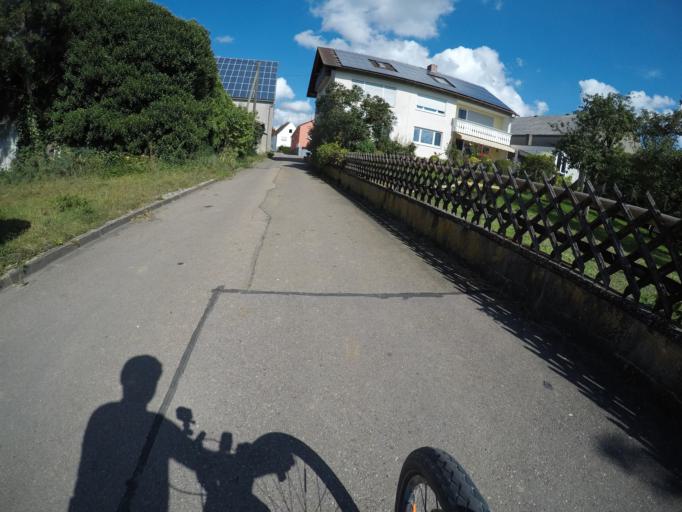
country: DE
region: Bavaria
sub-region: Swabia
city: Hochstadt an der Donau
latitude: 48.6178
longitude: 10.5365
